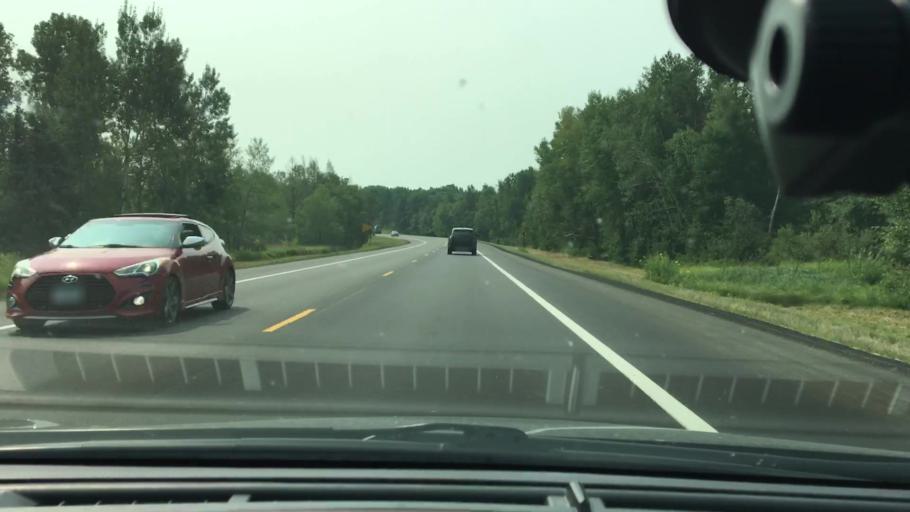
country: US
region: Minnesota
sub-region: Crow Wing County
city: Brainerd
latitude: 46.4201
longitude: -94.1788
